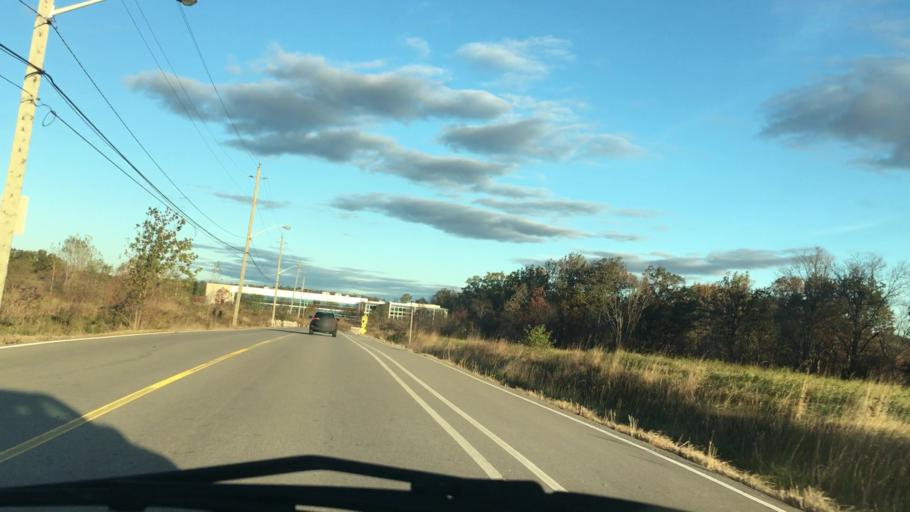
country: CA
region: Ontario
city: Burlington
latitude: 43.4322
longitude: -79.7871
